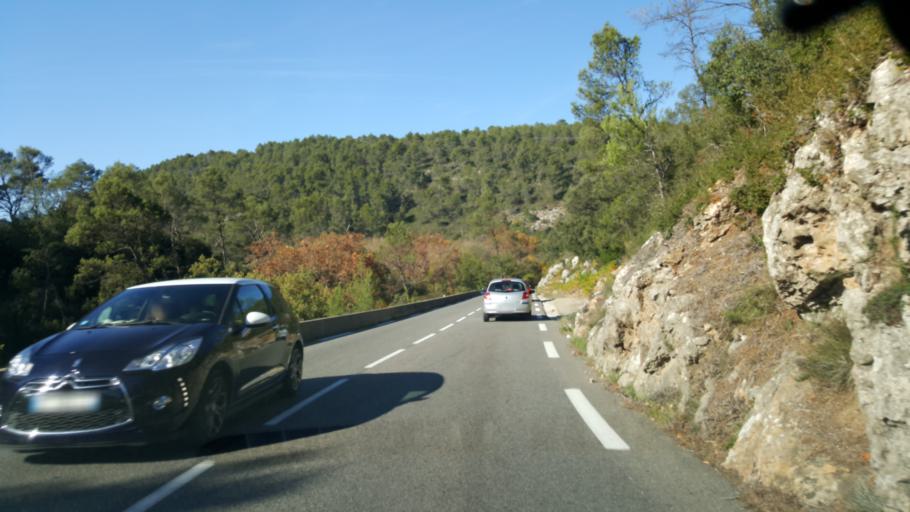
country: FR
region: Provence-Alpes-Cote d'Azur
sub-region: Departement du Var
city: Saint-Zacharie
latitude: 43.3831
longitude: 5.7363
